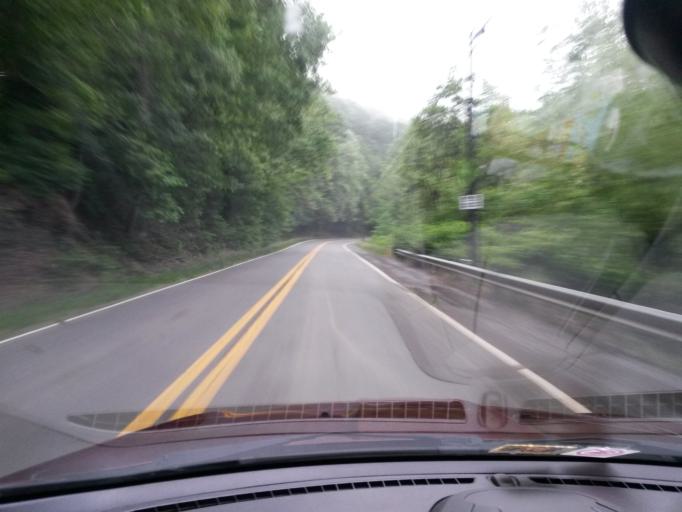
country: US
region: West Virginia
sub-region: Wyoming County
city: Pineville
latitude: 37.5270
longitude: -81.5920
